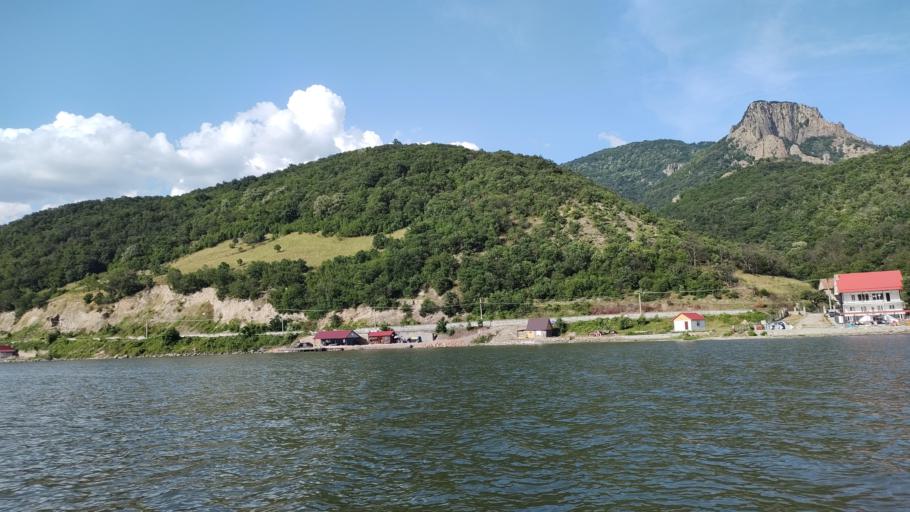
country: RO
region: Mehedinti
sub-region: Comuna Svinita
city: Svinita
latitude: 44.5596
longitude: 22.0315
